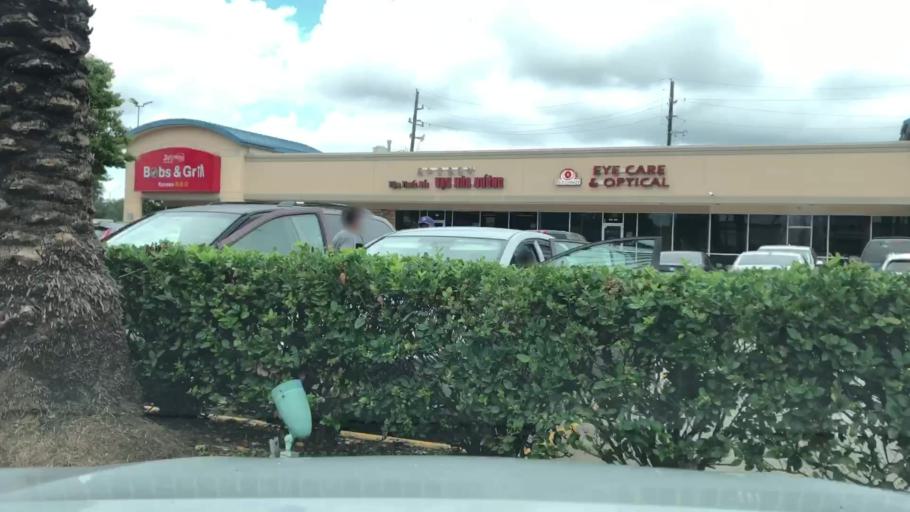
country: US
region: Texas
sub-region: Fort Bend County
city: Meadows Place
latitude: 29.6882
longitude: -95.5588
